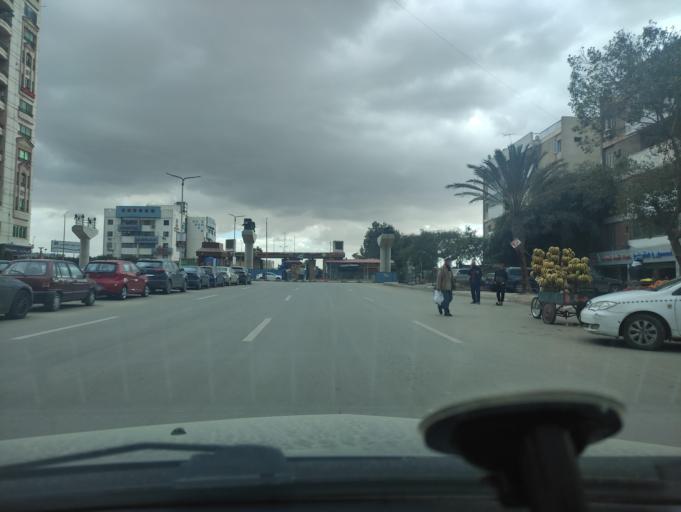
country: EG
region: Muhafazat al Qahirah
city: Cairo
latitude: 30.0469
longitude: 31.3513
